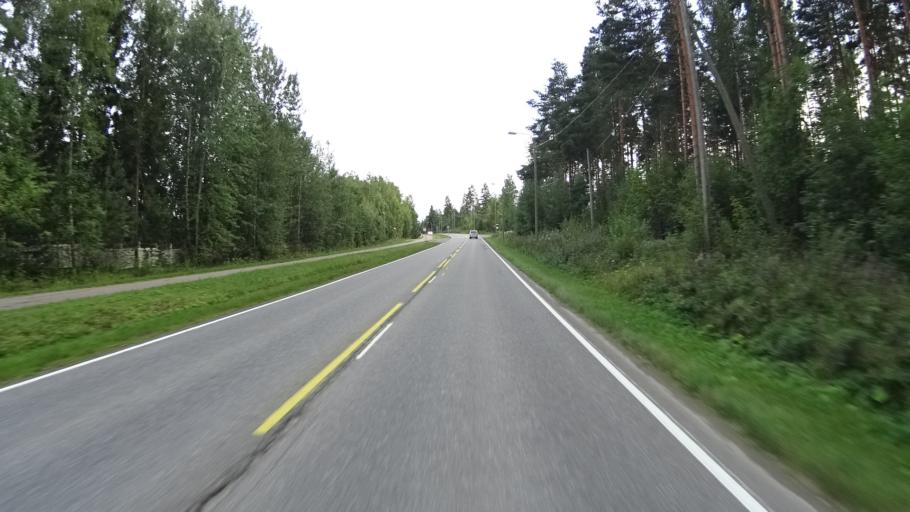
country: FI
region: Uusimaa
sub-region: Helsinki
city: Nurmijaervi
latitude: 60.3383
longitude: 24.8644
